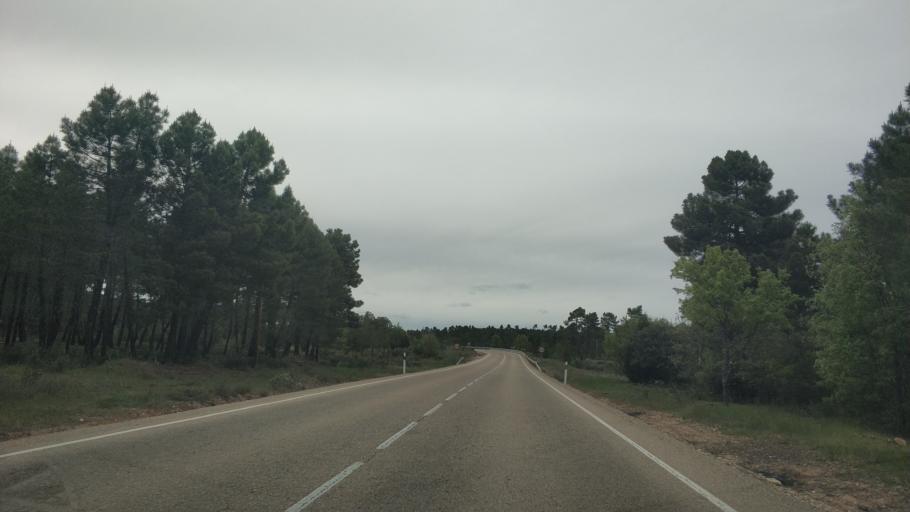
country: ES
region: Castille and Leon
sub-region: Provincia de Soria
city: Bayubas de Abajo
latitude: 41.5168
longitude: -2.9288
